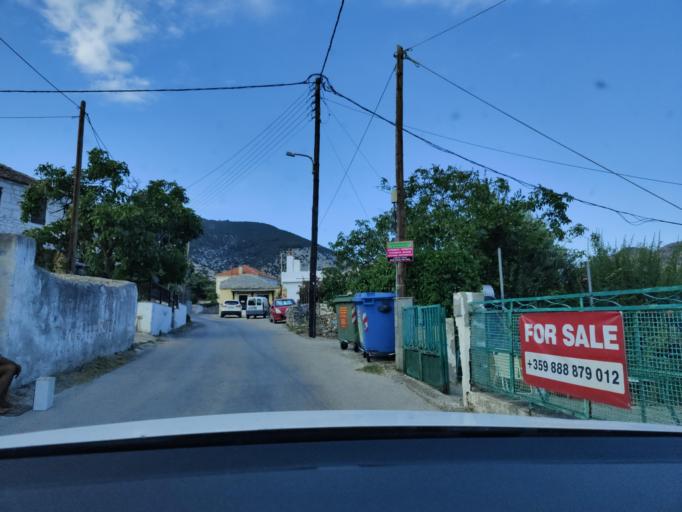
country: GR
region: East Macedonia and Thrace
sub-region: Nomos Kavalas
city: Potamia
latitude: 40.6578
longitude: 24.6898
